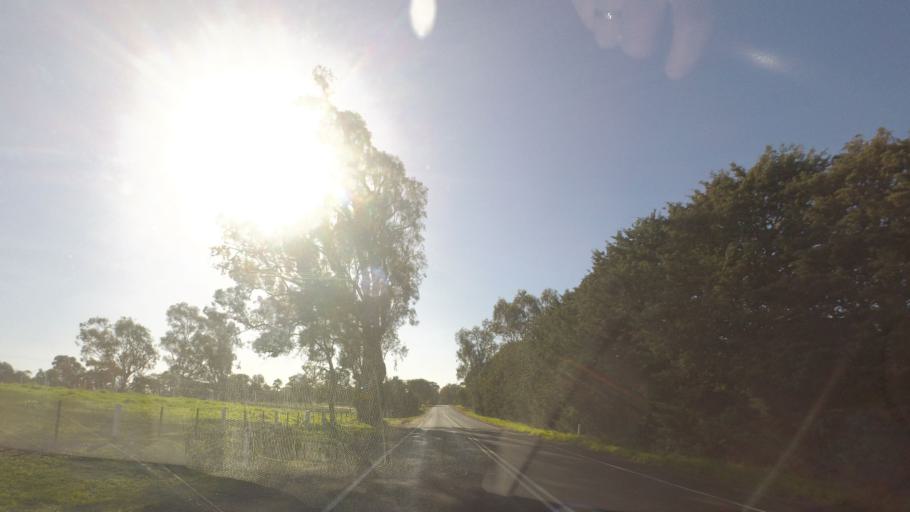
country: AU
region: Victoria
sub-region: Greater Bendigo
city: Kennington
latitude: -36.8813
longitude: 144.3131
